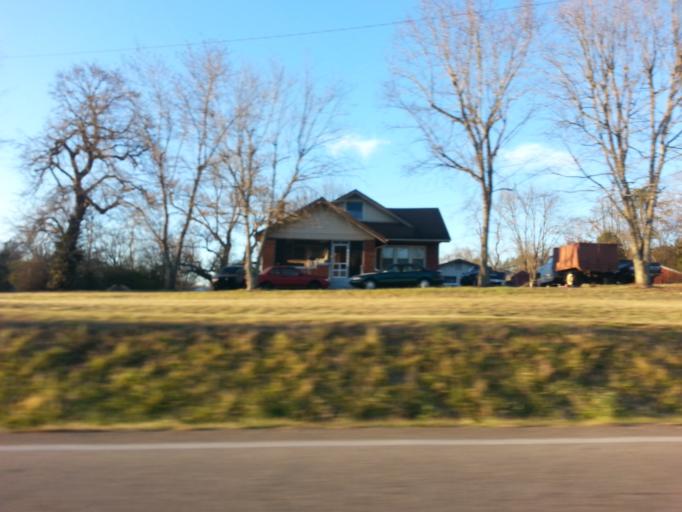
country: US
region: Tennessee
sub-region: Knox County
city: Mascot
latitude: 35.9872
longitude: -83.7973
